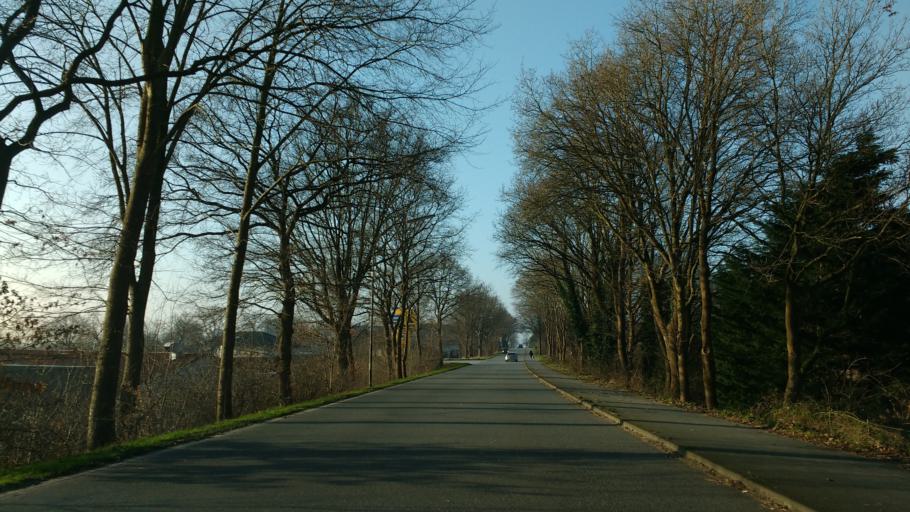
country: DE
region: Schleswig-Holstein
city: Wacken
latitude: 54.0213
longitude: 9.3870
